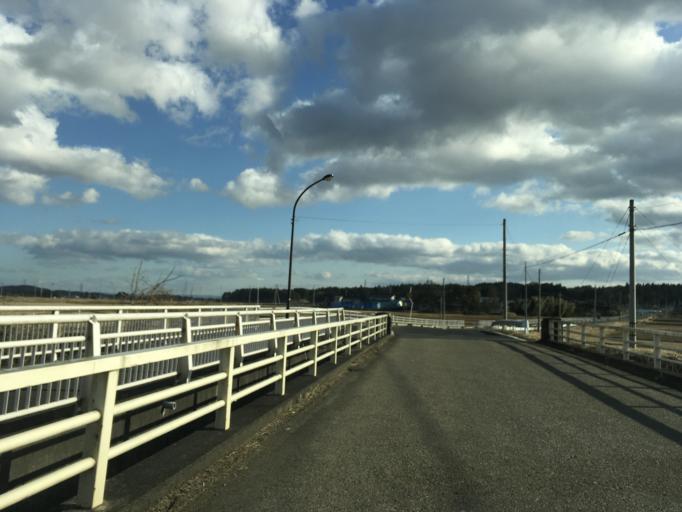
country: JP
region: Iwate
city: Ichinoseki
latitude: 38.8251
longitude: 141.0004
